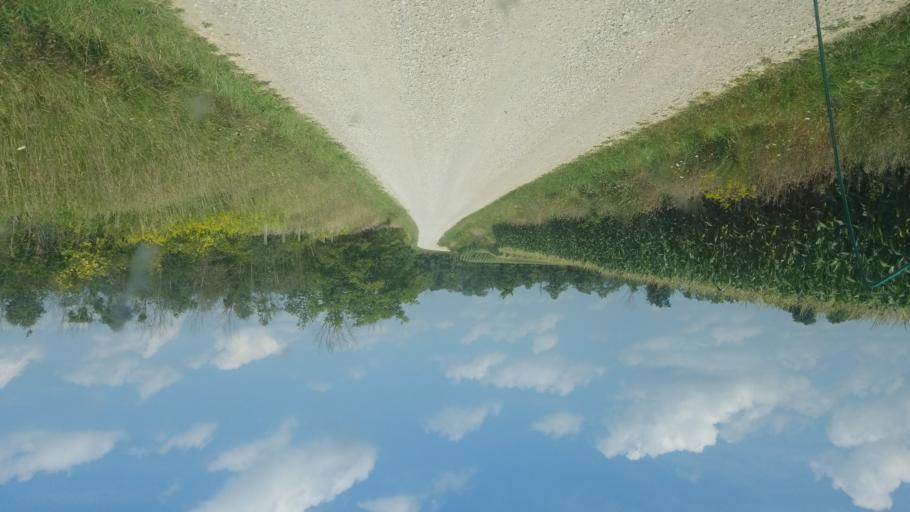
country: US
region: Ohio
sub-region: Huron County
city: New London
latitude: 40.9841
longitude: -82.4082
